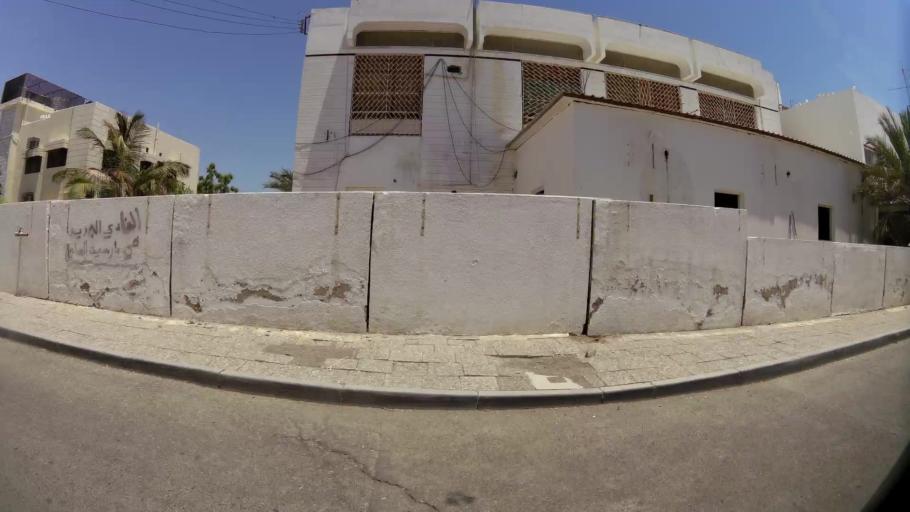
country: OM
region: Muhafazat Masqat
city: Muscat
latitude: 23.6049
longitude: 58.5421
